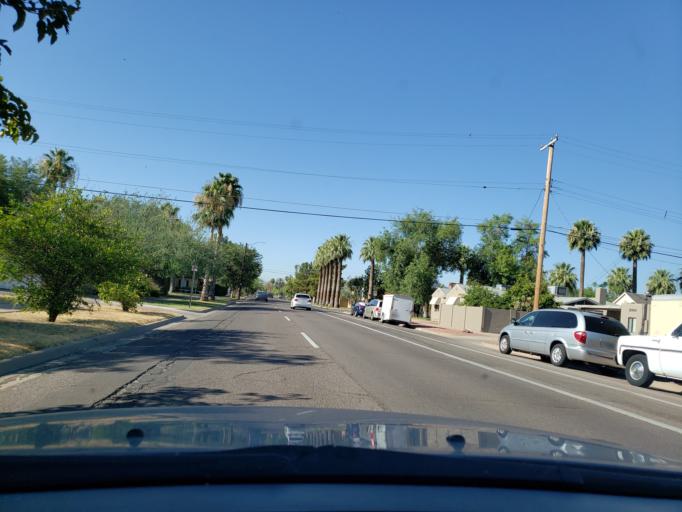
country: US
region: Arizona
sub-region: Maricopa County
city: Phoenix
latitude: 33.4701
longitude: -112.0803
